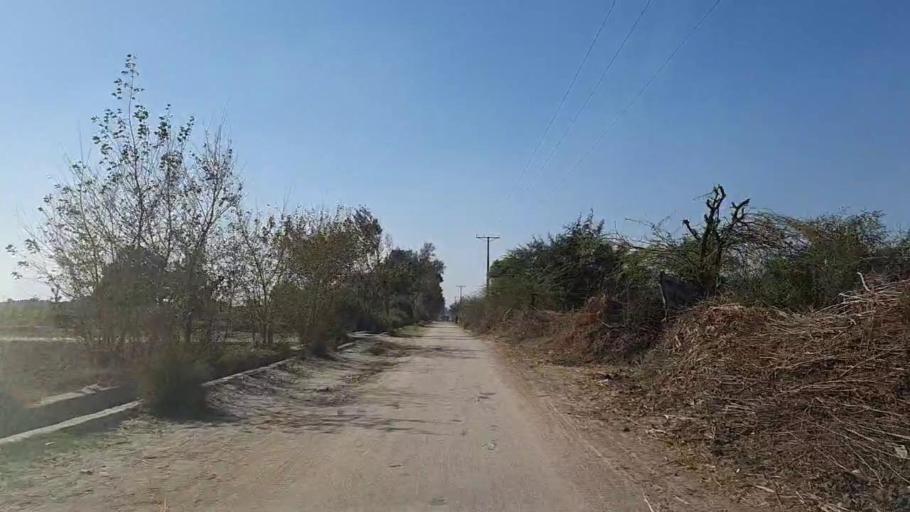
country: PK
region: Sindh
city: Nawabshah
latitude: 26.2444
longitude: 68.4320
